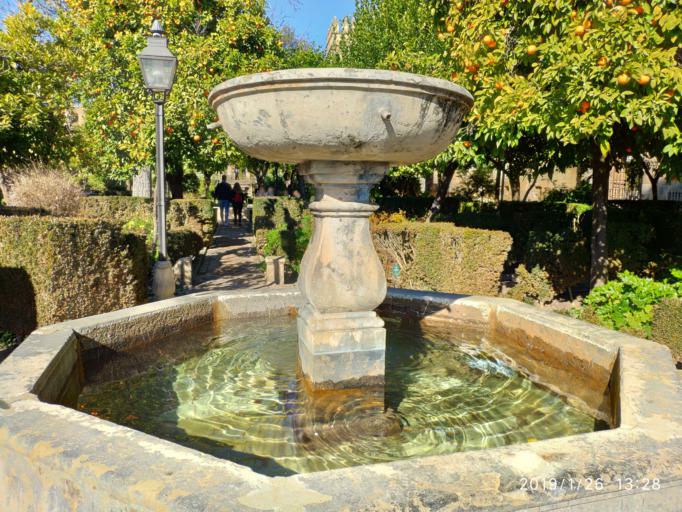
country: ES
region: Andalusia
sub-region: Province of Cordoba
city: Cordoba
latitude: 37.8761
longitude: -4.7816
